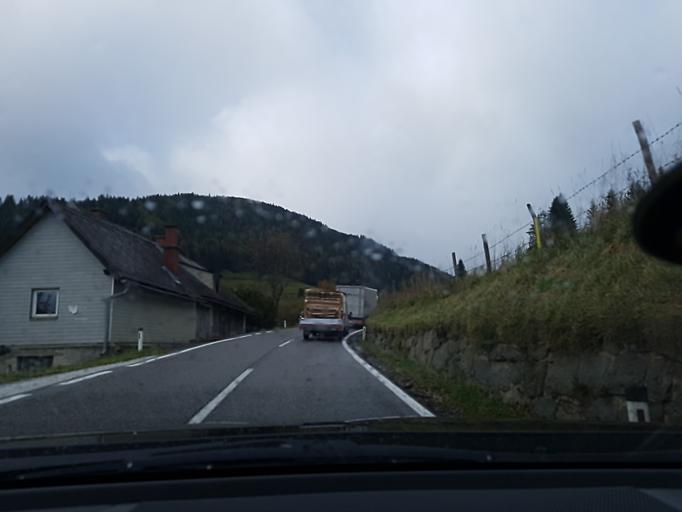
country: AT
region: Styria
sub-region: Politischer Bezirk Murtal
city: Sankt Johann am Tauern
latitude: 47.3458
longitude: 14.4723
